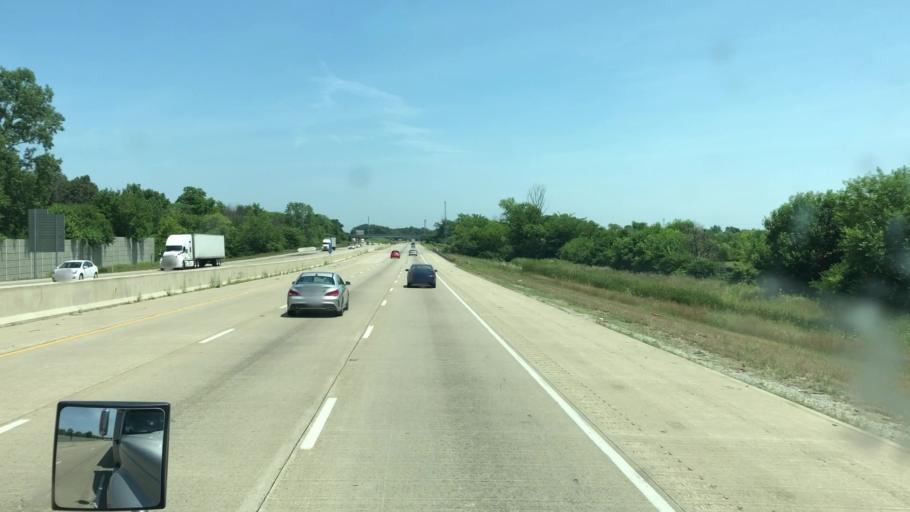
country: US
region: Indiana
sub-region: Marion County
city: Cumberland
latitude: 39.8025
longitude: -85.9790
